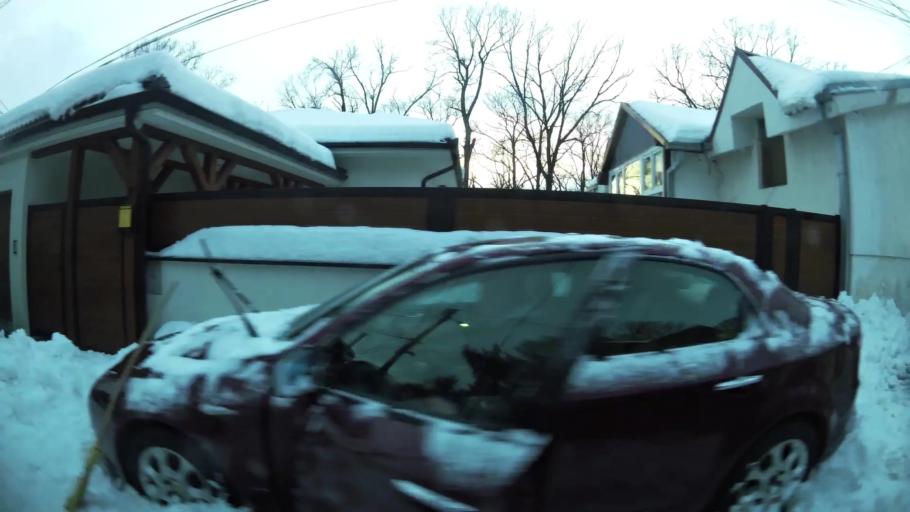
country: RS
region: Central Serbia
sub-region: Belgrade
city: Palilula
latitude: 44.8008
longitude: 20.5064
